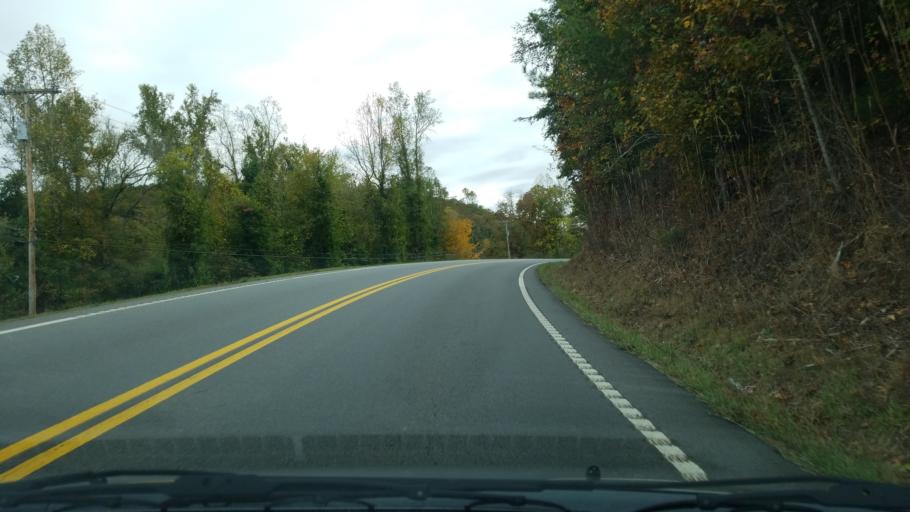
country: US
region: Tennessee
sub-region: Bradley County
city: Hopewell
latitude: 35.3394
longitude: -84.9712
